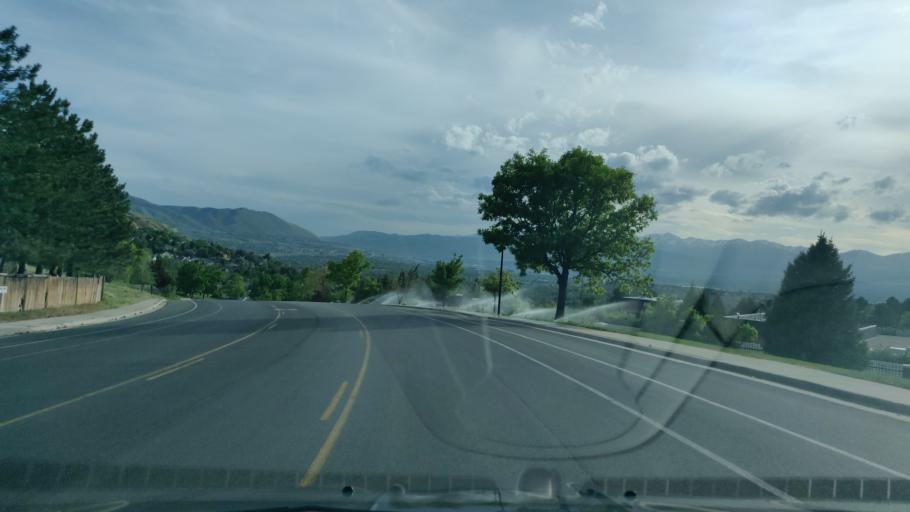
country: US
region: Utah
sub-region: Salt Lake County
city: Granite
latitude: 40.5403
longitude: -111.8173
